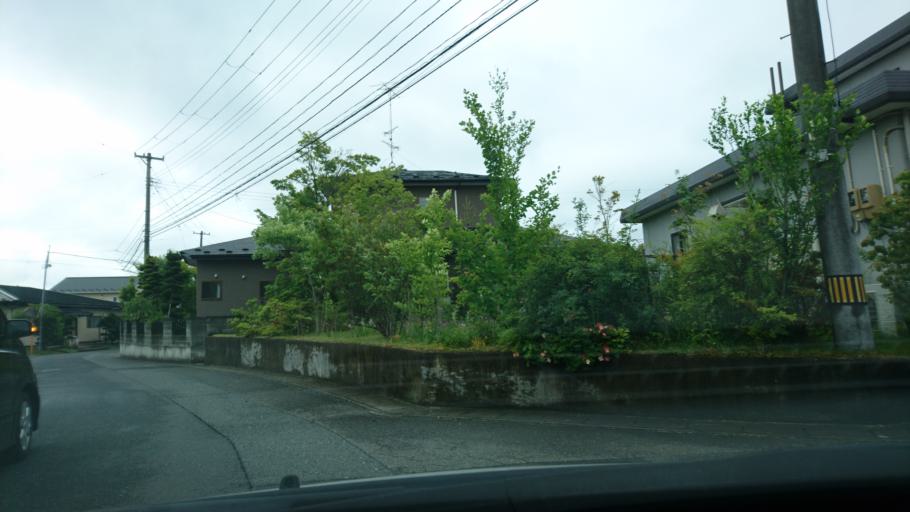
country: JP
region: Iwate
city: Ichinoseki
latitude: 38.9100
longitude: 141.1388
